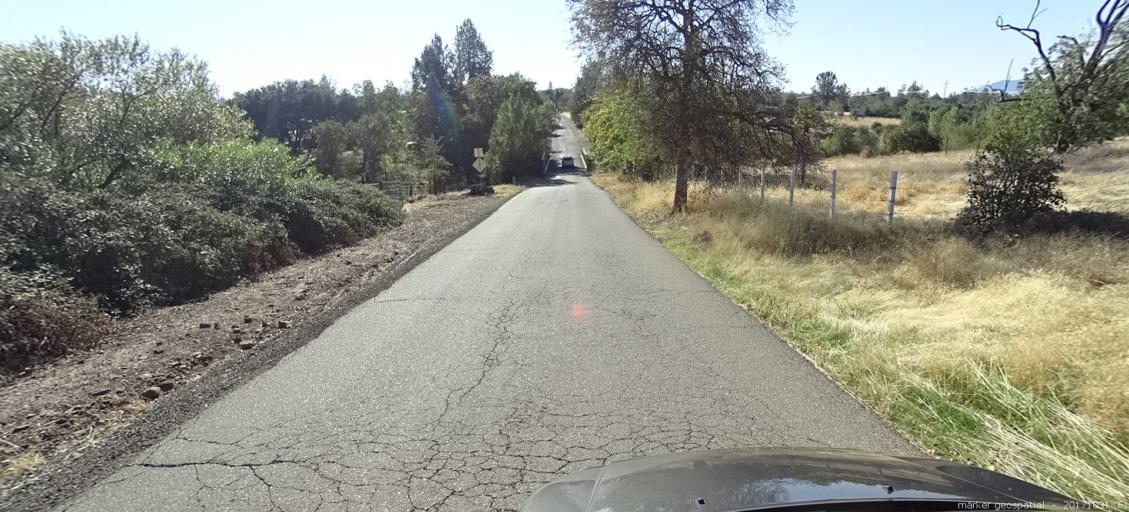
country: US
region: California
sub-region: Shasta County
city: Shingletown
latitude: 40.4379
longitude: -121.8710
